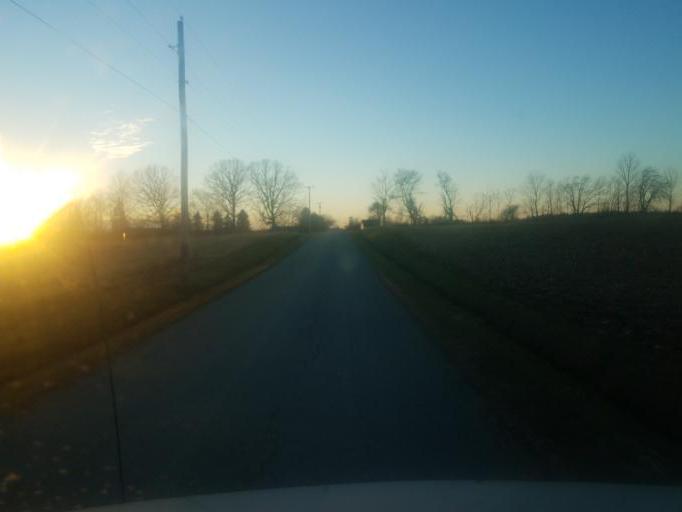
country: US
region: Ohio
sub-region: Richland County
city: Ontario
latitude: 40.8432
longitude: -82.5601
